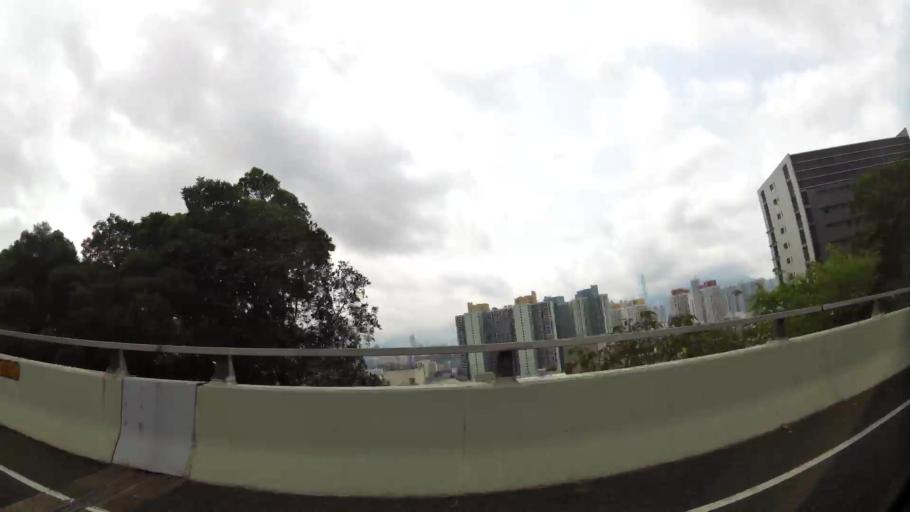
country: HK
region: Sham Shui Po
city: Sham Shui Po
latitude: 22.3403
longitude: 114.1673
